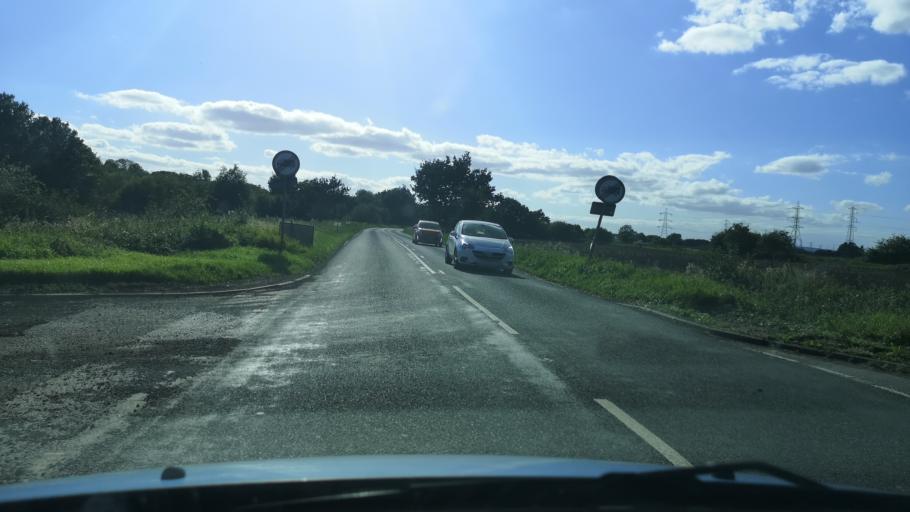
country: GB
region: England
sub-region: Doncaster
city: Kirk Sandall
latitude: 53.5730
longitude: -1.0902
